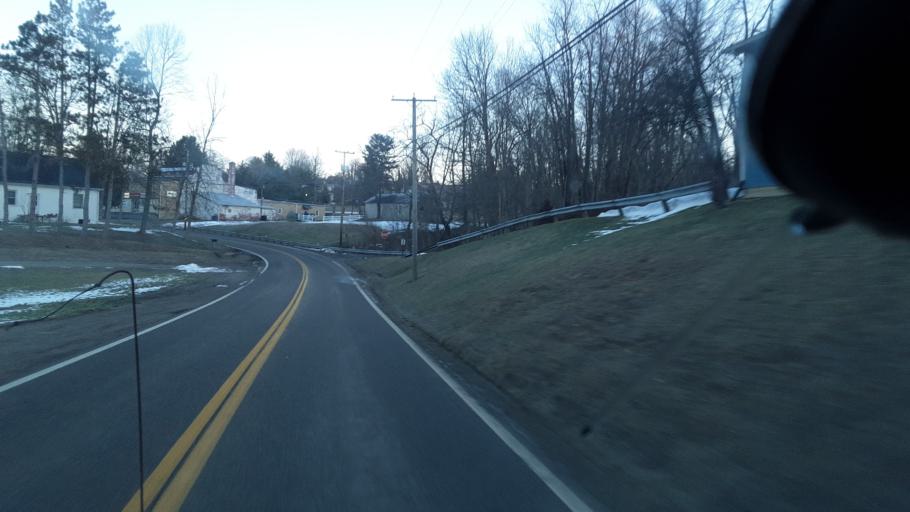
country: US
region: Ohio
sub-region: Perry County
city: Somerset
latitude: 39.8024
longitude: -82.2997
